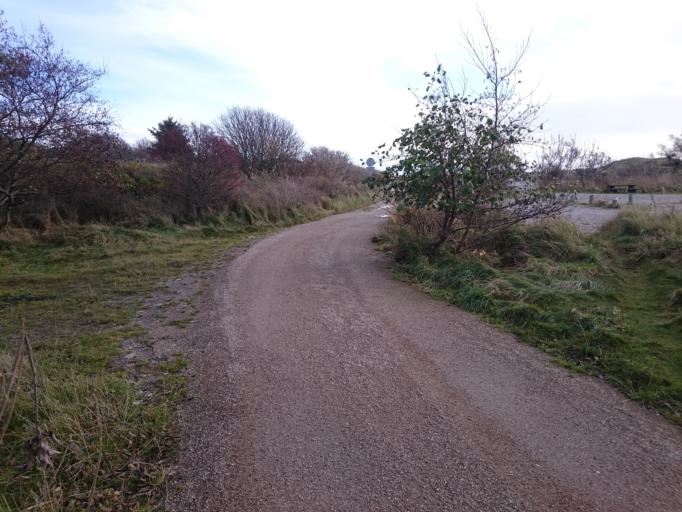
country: DK
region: North Denmark
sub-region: Frederikshavn Kommune
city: Skagen
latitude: 57.7401
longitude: 10.6296
